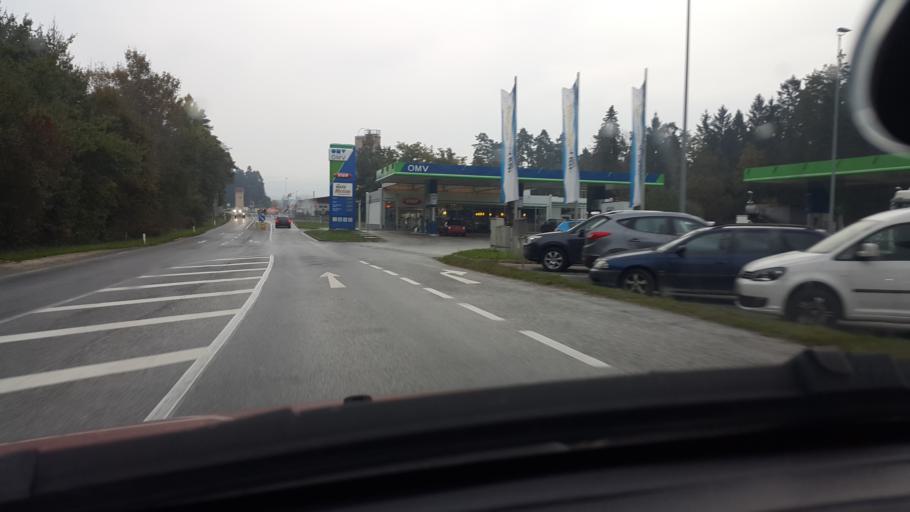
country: AT
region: Carinthia
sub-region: Politischer Bezirk Klagenfurt Land
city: Poggersdorf
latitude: 46.6390
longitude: 14.4506
